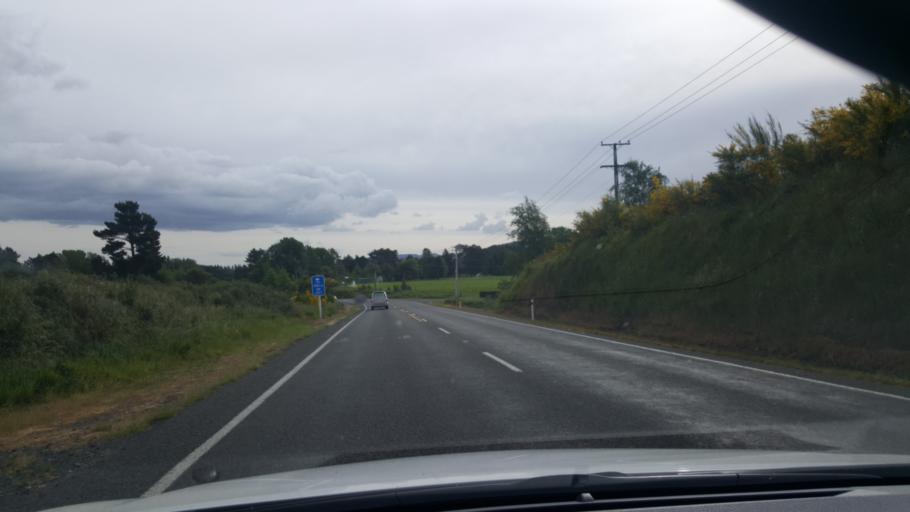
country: NZ
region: Waikato
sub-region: Taupo District
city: Taupo
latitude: -38.4822
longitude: 176.2942
